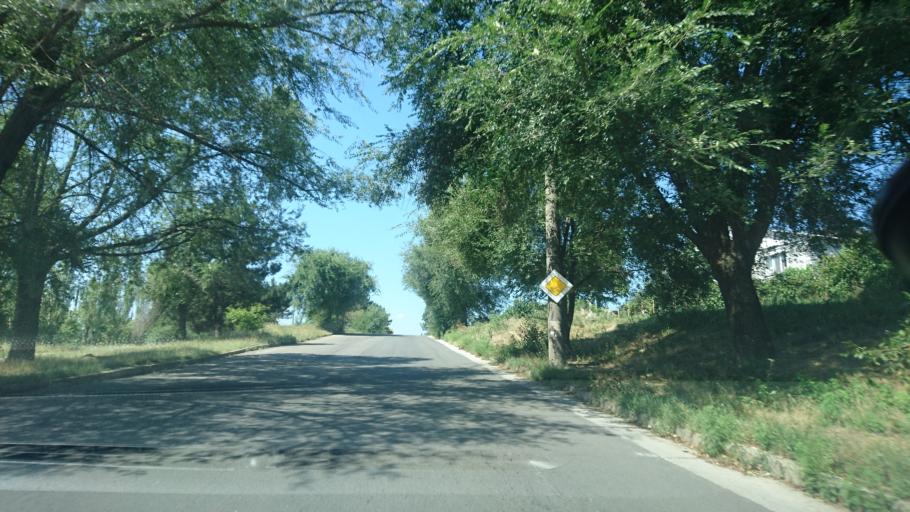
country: MD
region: Laloveni
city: Ialoveni
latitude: 46.9947
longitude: 28.7965
